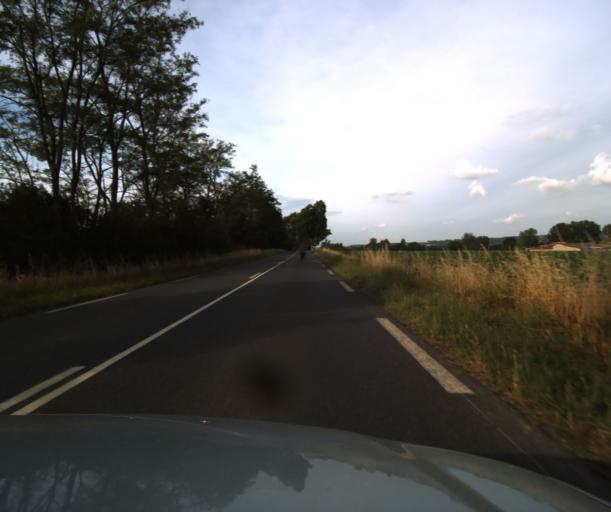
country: FR
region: Midi-Pyrenees
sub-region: Departement du Tarn-et-Garonne
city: Beaumont-de-Lomagne
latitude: 43.9108
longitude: 1.0476
